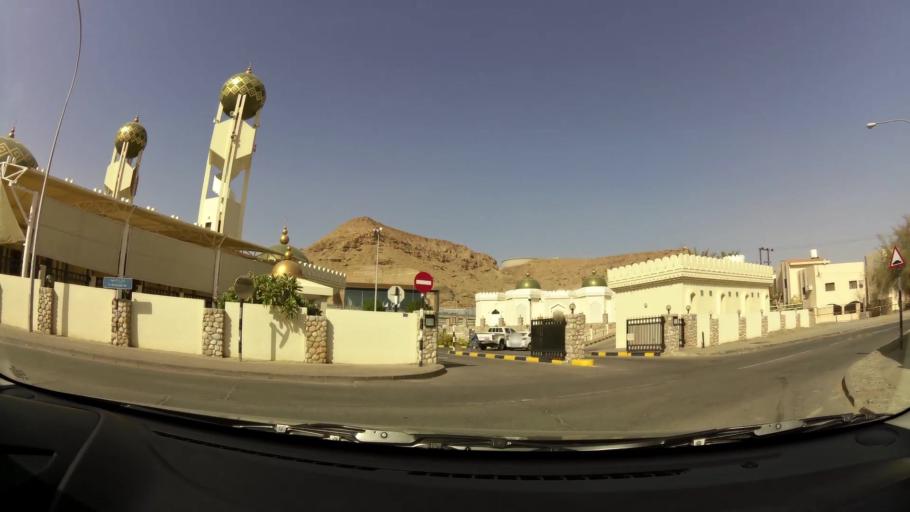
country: OM
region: Muhafazat Masqat
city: Muscat
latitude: 23.6048
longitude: 58.5111
